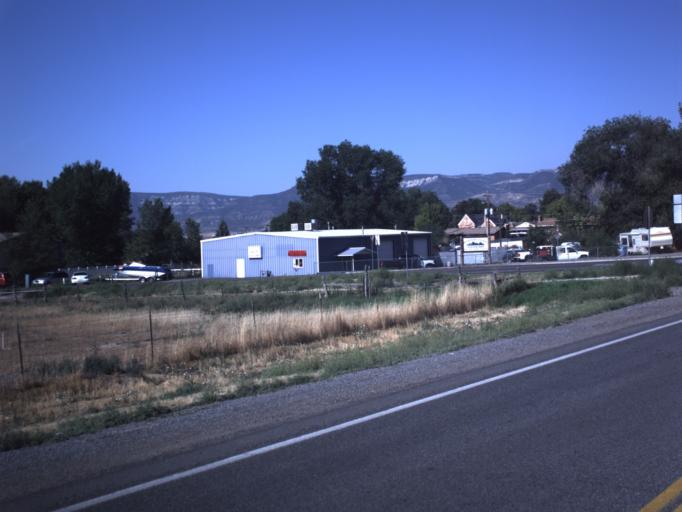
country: US
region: Utah
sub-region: Sanpete County
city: Moroni
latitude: 39.5249
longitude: -111.5756
